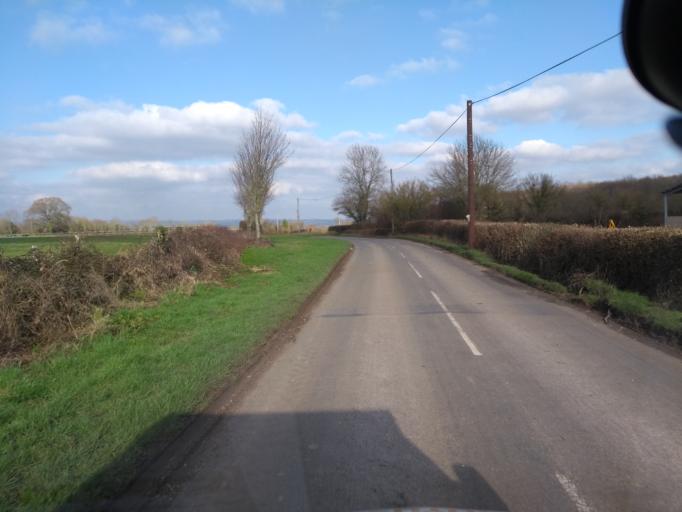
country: GB
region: England
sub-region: Somerset
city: Creech Saint Michael
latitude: 50.9688
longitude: -3.0531
